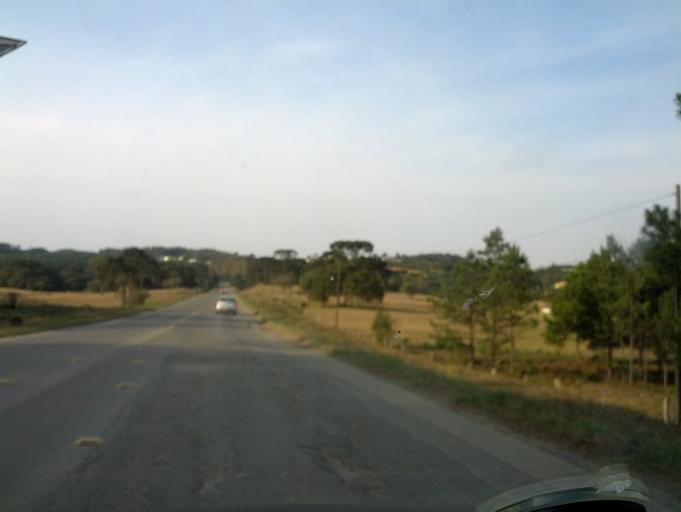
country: BR
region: Santa Catarina
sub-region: Otacilio Costa
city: Otacilio Costa
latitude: -27.5771
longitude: -50.1578
